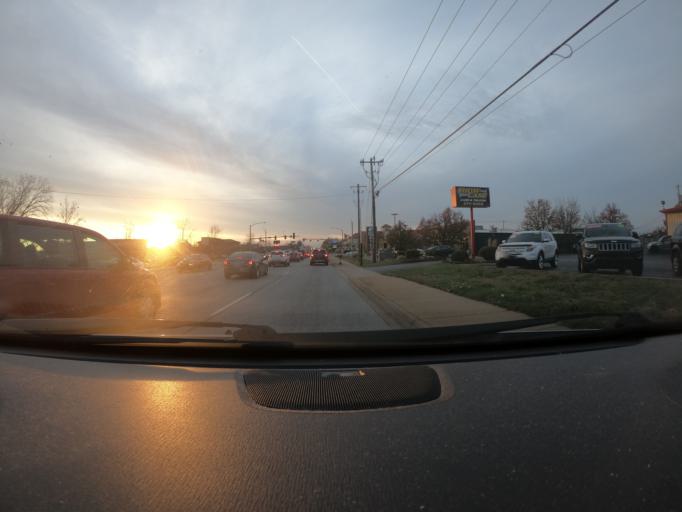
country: US
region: Arkansas
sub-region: Benton County
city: Bentonville
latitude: 36.3354
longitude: -94.1961
